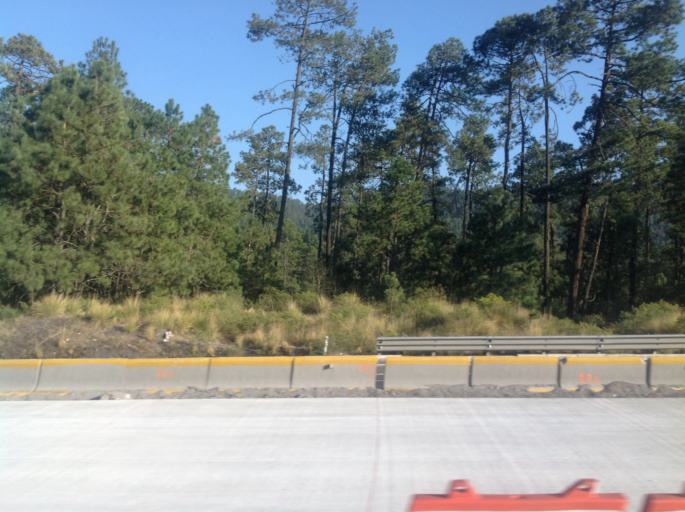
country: MX
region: Mexico
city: Rio Frio de Juarez
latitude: 19.3375
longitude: -98.6735
